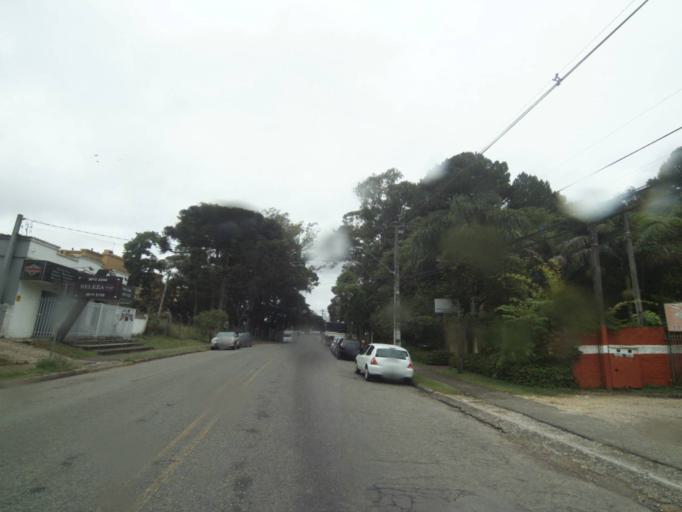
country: BR
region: Parana
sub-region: Curitiba
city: Curitiba
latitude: -25.4467
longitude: -49.3483
